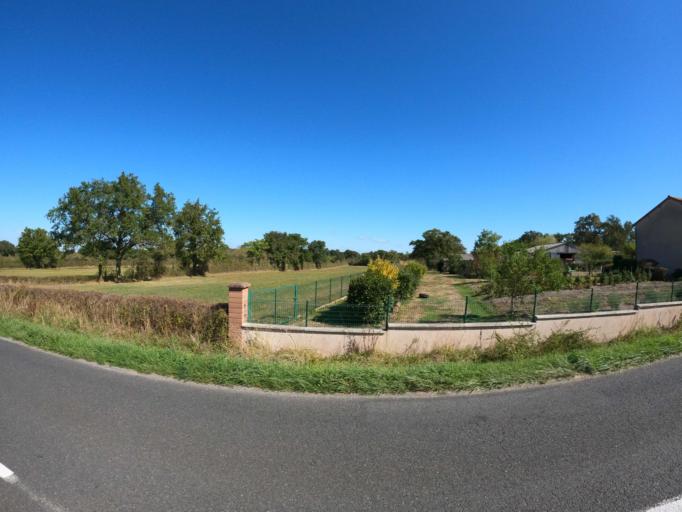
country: FR
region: Poitou-Charentes
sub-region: Departement de la Vienne
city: Lathus-Saint-Remy
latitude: 46.3015
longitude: 0.9919
